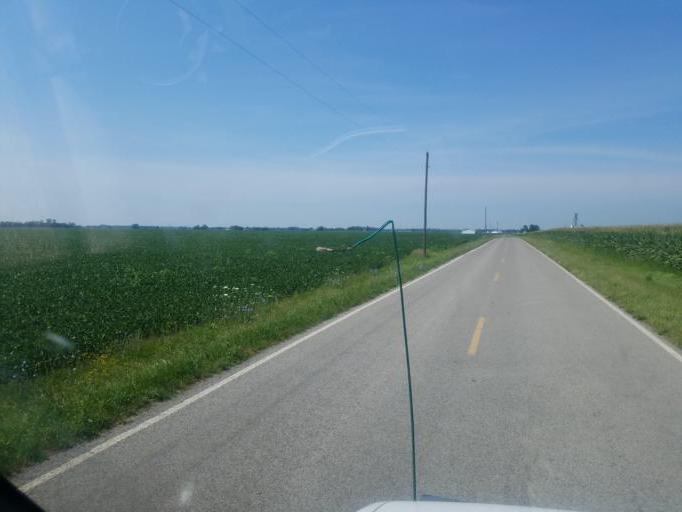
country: US
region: Ohio
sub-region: Champaign County
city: North Lewisburg
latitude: 40.2065
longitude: -83.4986
